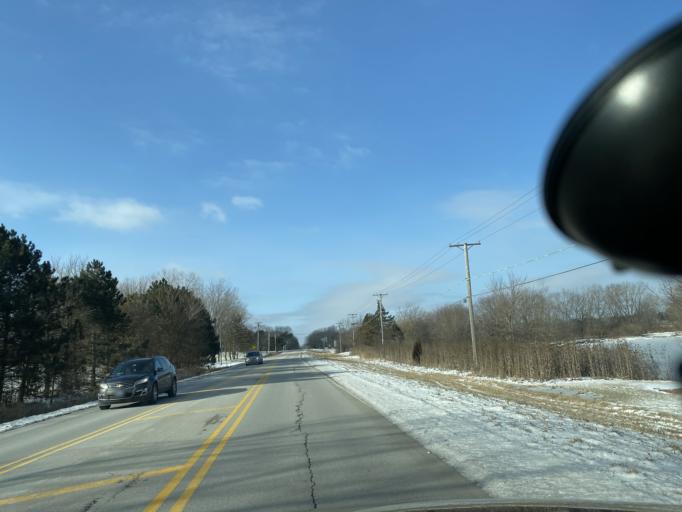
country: US
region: Illinois
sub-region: Will County
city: Goodings Grove
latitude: 41.6503
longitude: -87.9565
